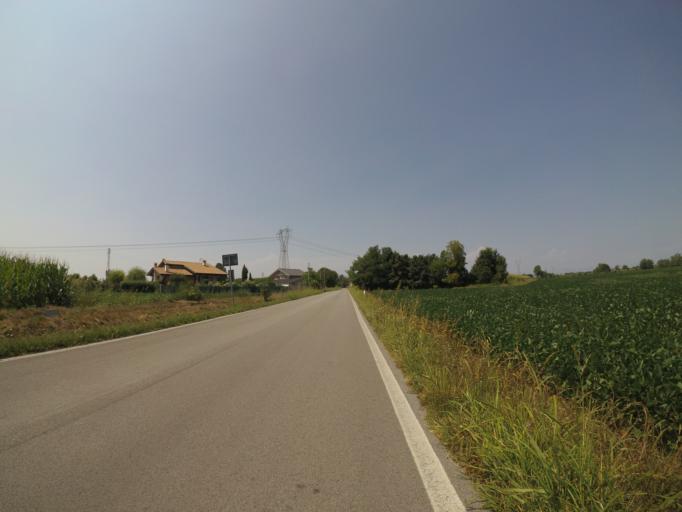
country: IT
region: Friuli Venezia Giulia
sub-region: Provincia di Udine
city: Castions di Strada
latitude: 45.9149
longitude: 13.1676
